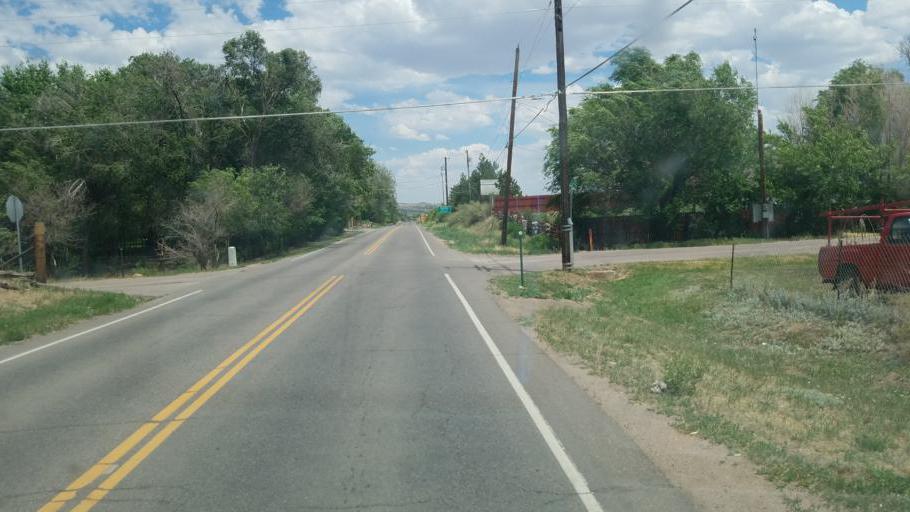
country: US
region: Colorado
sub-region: Fremont County
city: Lincoln Park
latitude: 38.4175
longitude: -105.1953
